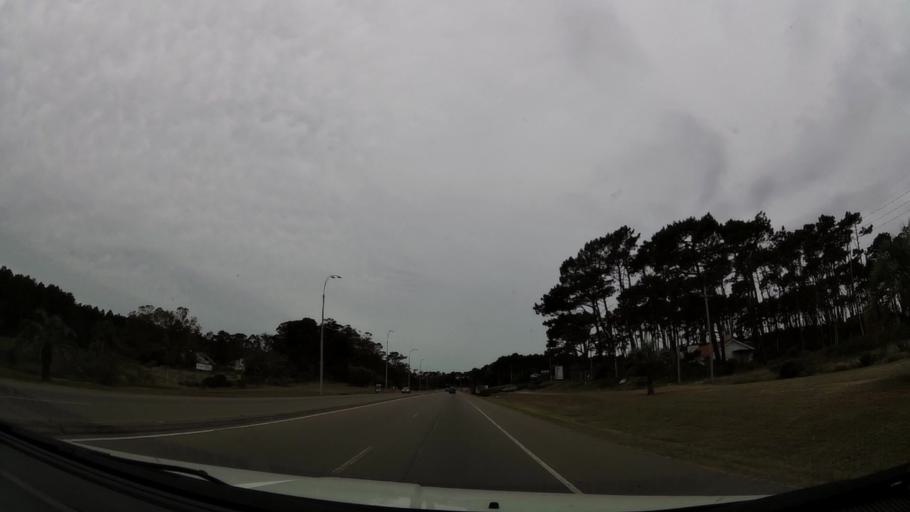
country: UY
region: Maldonado
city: Maldonado
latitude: -34.9049
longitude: -55.0288
